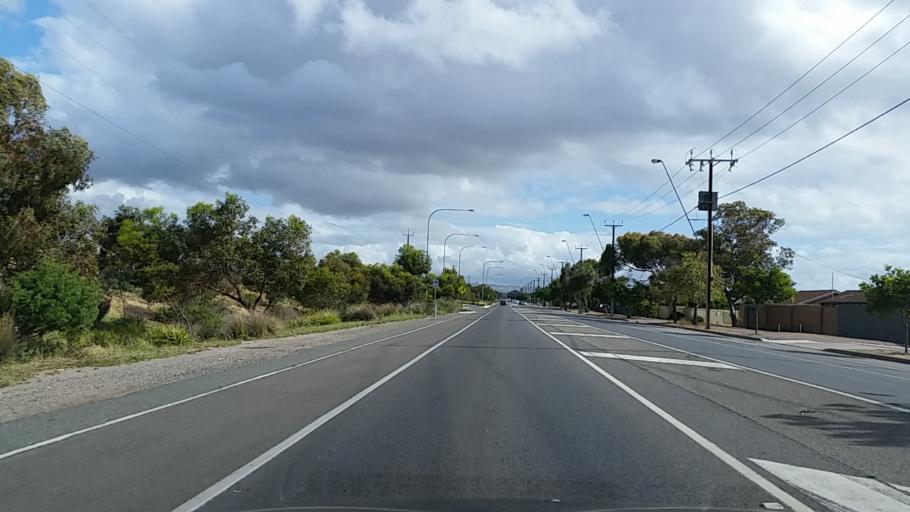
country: AU
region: South Australia
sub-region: Onkaparinga
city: Seaford
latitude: -35.1745
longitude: 138.4763
